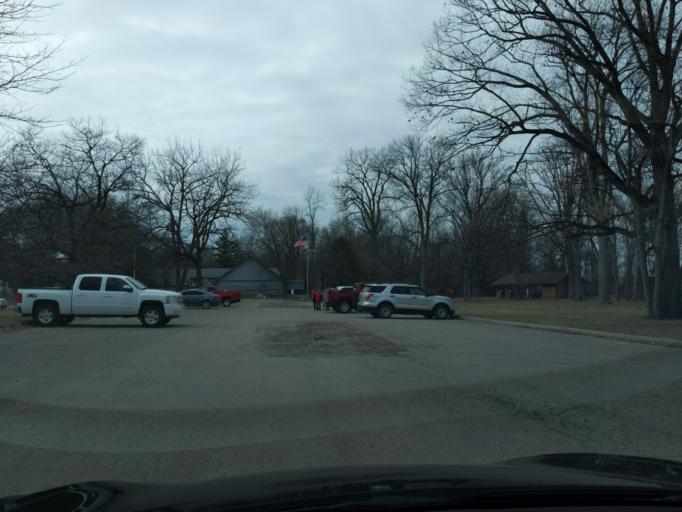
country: US
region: Michigan
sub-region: Bay County
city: Bay City
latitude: 43.6695
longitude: -83.9101
